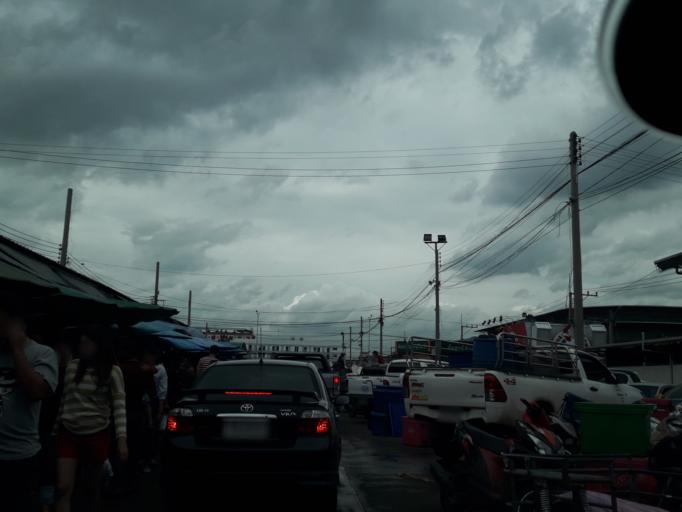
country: TH
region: Pathum Thani
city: Khlong Luang
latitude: 14.0805
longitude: 100.6213
